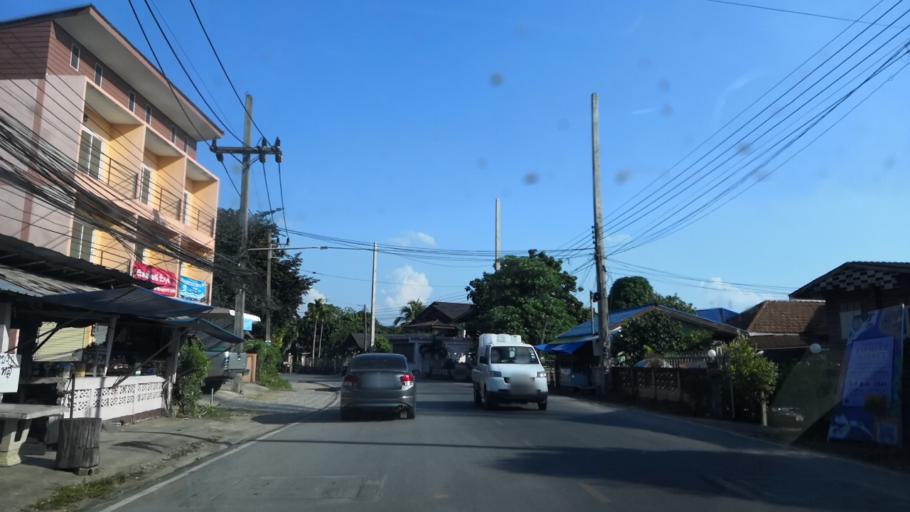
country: TH
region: Chiang Rai
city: Chiang Rai
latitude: 19.9287
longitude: 99.8467
